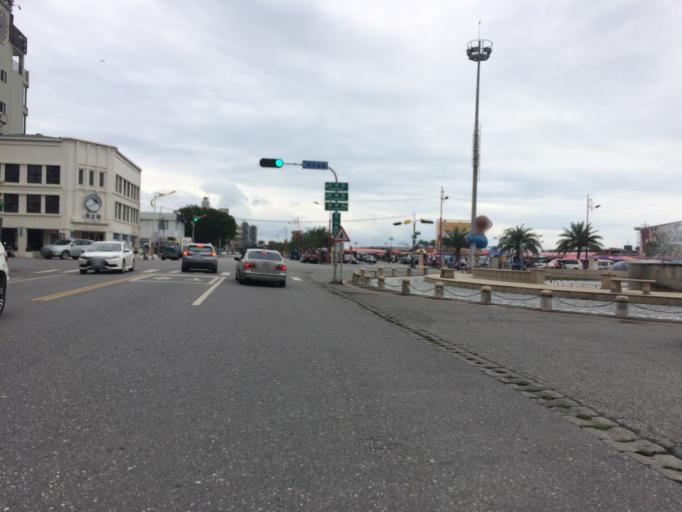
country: TW
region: Taiwan
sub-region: Hualien
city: Hualian
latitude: 23.9746
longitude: 121.6112
